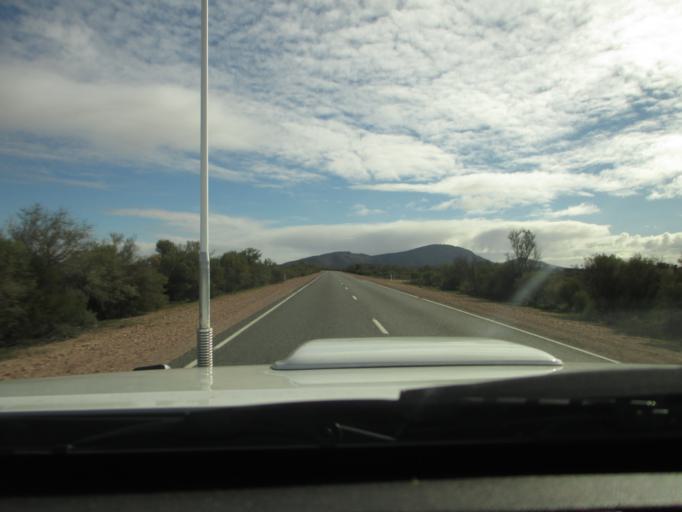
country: AU
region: South Australia
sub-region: Flinders Ranges
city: Quorn
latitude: -31.8278
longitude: 138.3836
